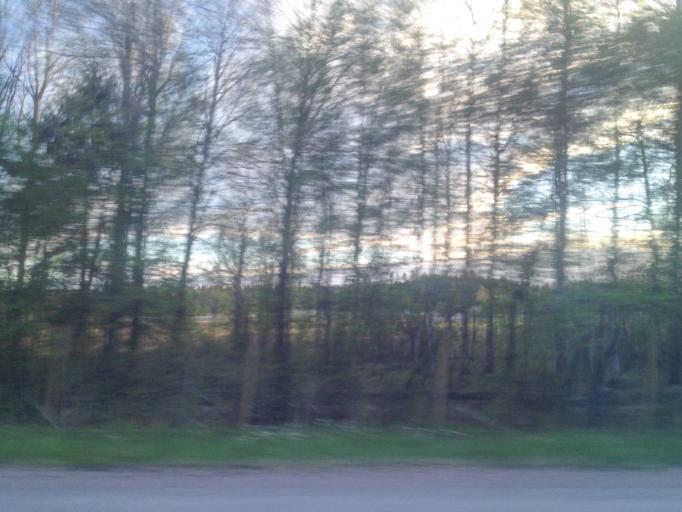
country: FI
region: Haeme
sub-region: Riihimaeki
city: Riihimaeki
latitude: 60.7304
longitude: 24.7265
